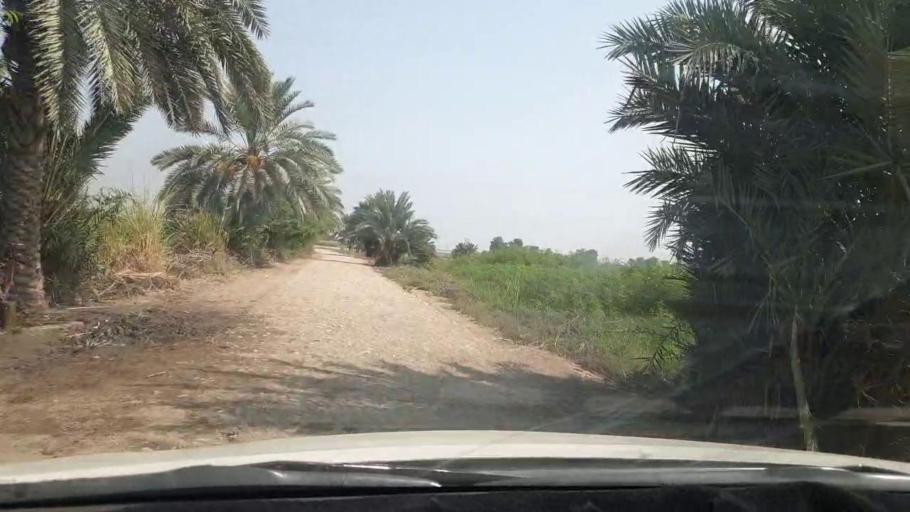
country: PK
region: Sindh
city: Rohri
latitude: 27.6322
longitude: 68.8853
